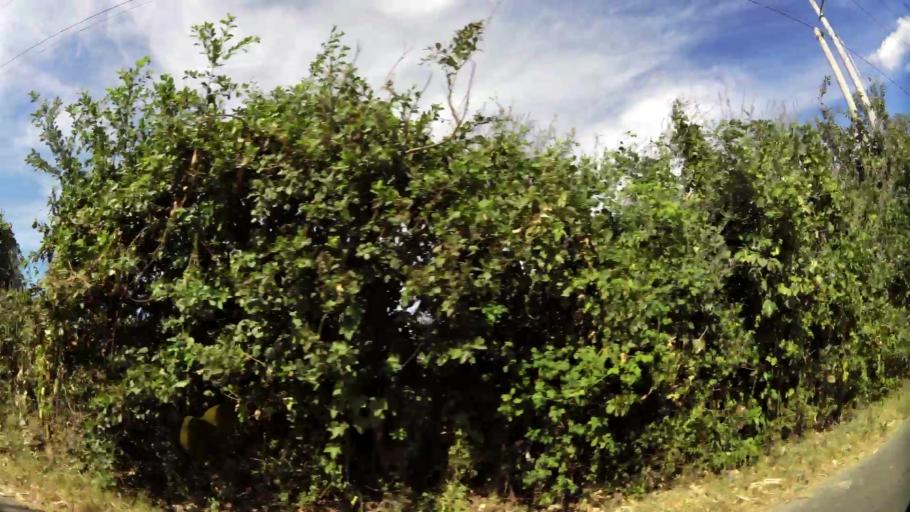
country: SV
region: San Salvador
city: Aguilares
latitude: 13.9608
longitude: -89.1586
